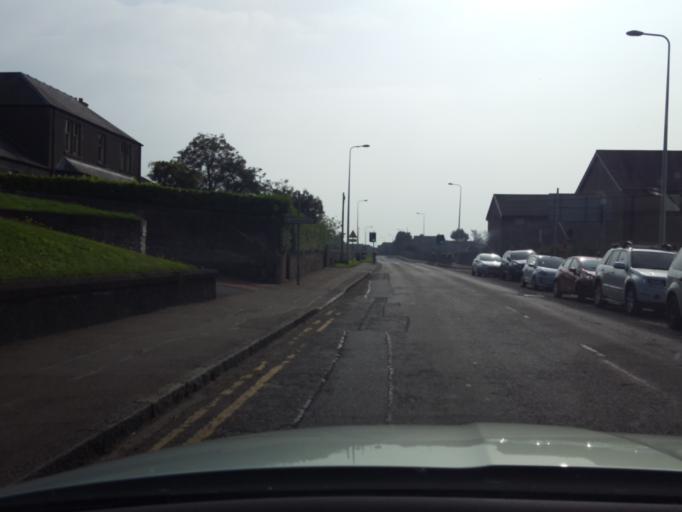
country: GB
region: Scotland
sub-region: Fife
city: Crossgates
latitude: 56.0834
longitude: -3.3755
